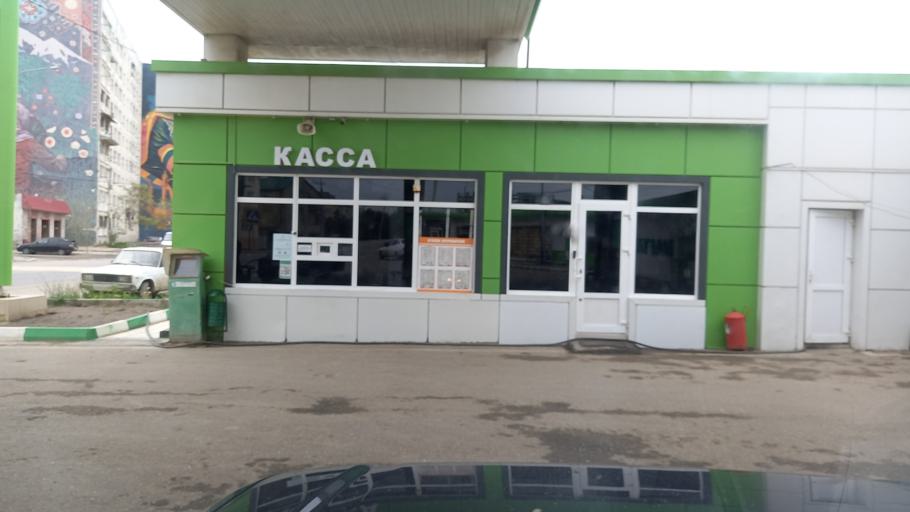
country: RU
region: Dagestan
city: Derbent
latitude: 42.0739
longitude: 48.2996
